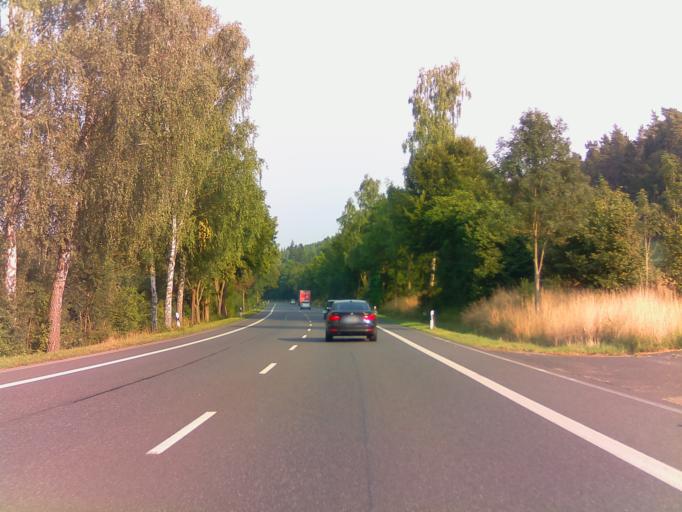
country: DE
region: Hesse
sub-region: Regierungsbezirk Kassel
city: Schenklengsfeld
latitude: 50.8621
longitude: 9.7905
